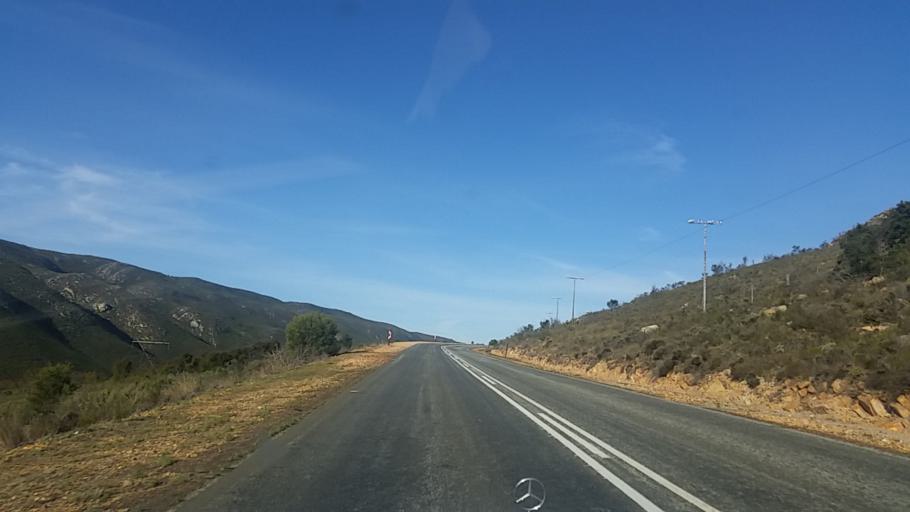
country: ZA
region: Western Cape
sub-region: Eden District Municipality
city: Knysna
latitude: -33.7498
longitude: 22.9681
